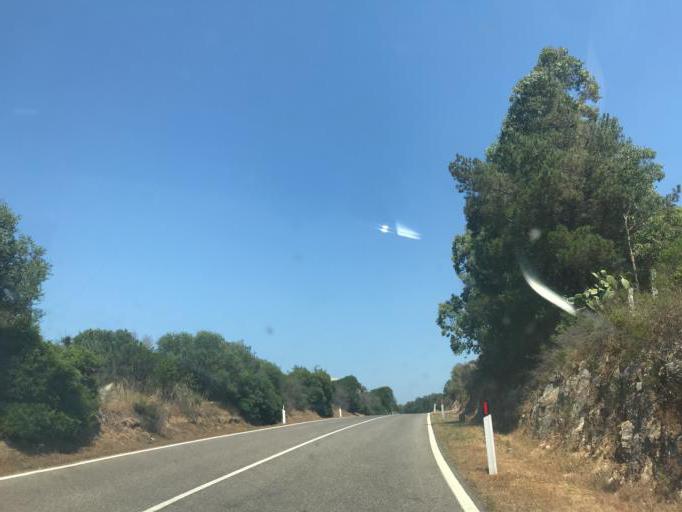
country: IT
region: Sardinia
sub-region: Provincia di Olbia-Tempio
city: Arzachena
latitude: 41.0296
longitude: 9.3699
